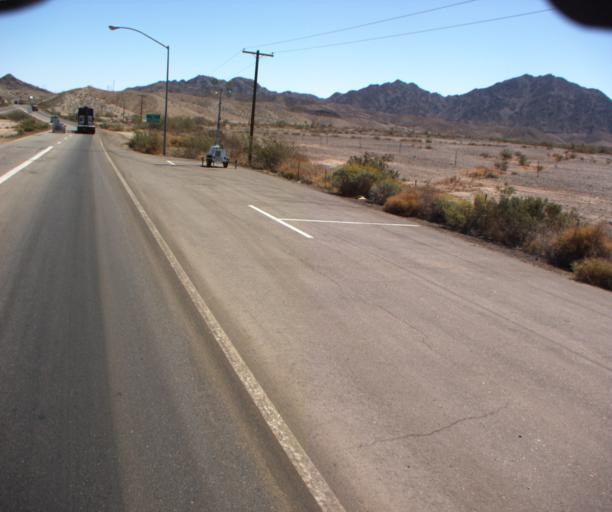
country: US
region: Arizona
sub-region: Yuma County
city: Fortuna Foothills
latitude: 32.6596
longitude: -114.3638
